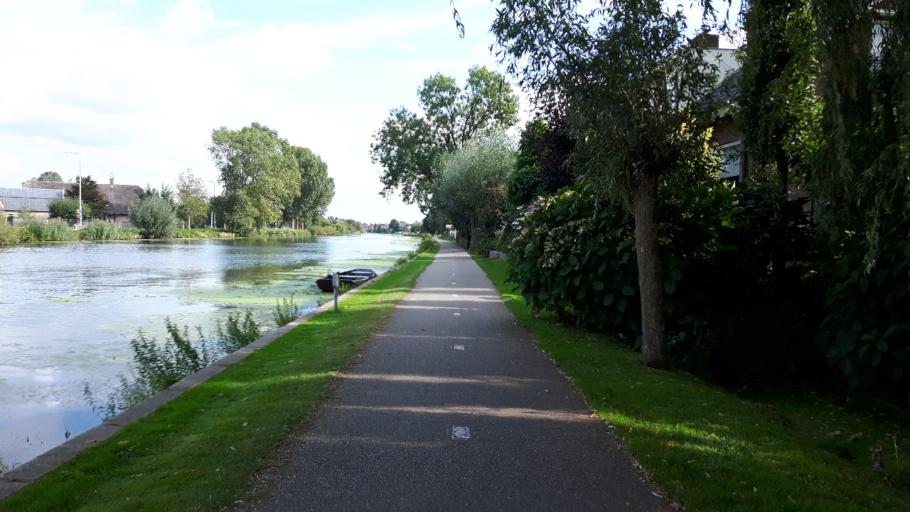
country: NL
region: South Holland
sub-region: Bodegraven-Reeuwijk
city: Bodegraven
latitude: 52.0828
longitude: 4.8009
